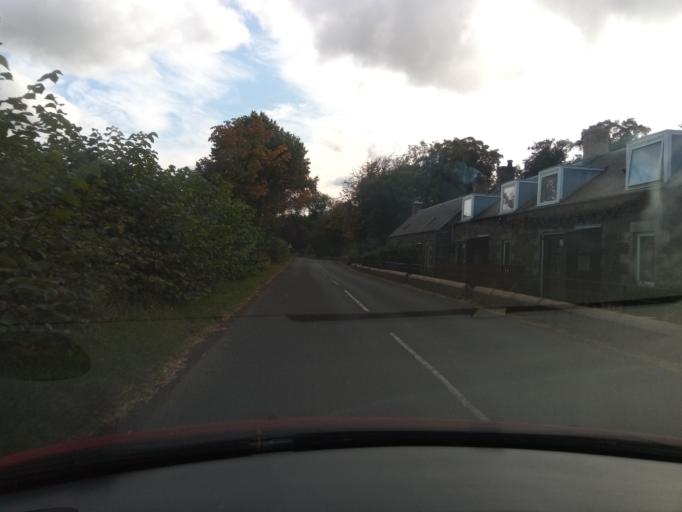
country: GB
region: Scotland
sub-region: The Scottish Borders
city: Kelso
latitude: 55.5228
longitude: -2.3561
